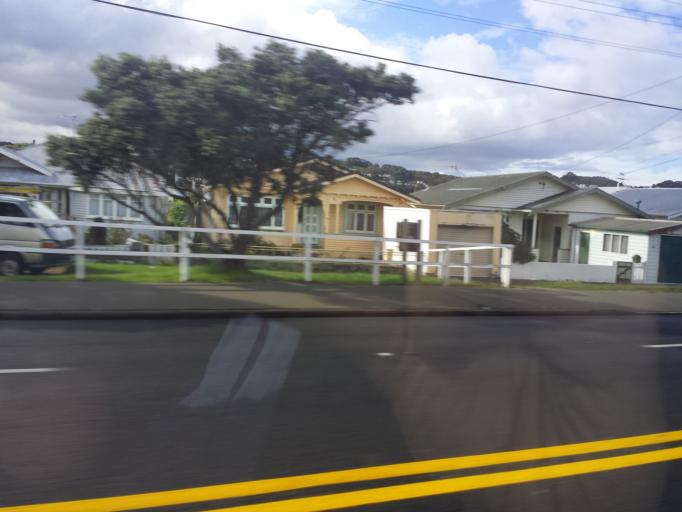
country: NZ
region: Wellington
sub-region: Wellington City
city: Wellington
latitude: -41.3215
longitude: 174.8091
